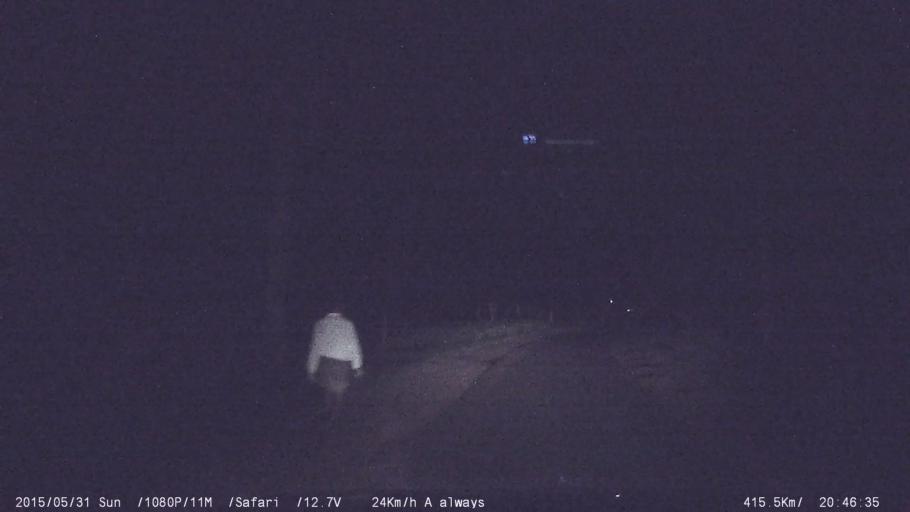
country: IN
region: Karnataka
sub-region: Ramanagara
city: Channapatna
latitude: 12.5590
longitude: 77.2202
